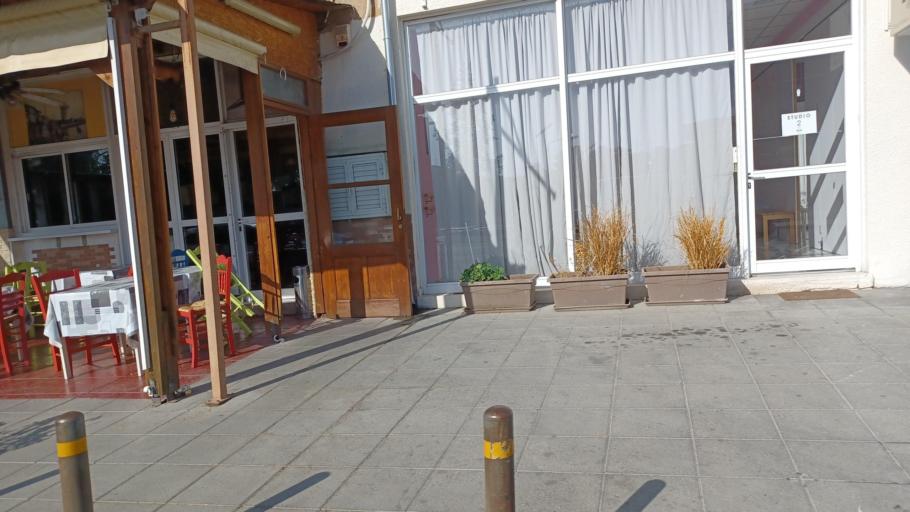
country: CY
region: Lefkosia
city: Alampra
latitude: 34.9961
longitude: 33.3671
